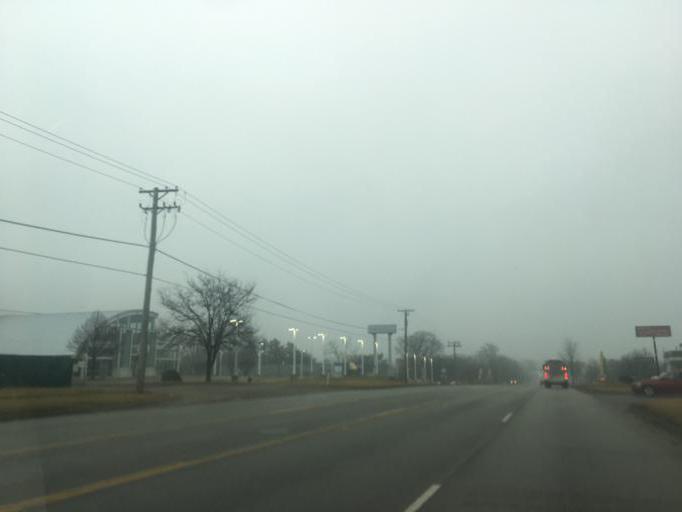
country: US
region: Illinois
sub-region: DuPage County
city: Naperville
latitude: 41.7963
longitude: -88.1151
